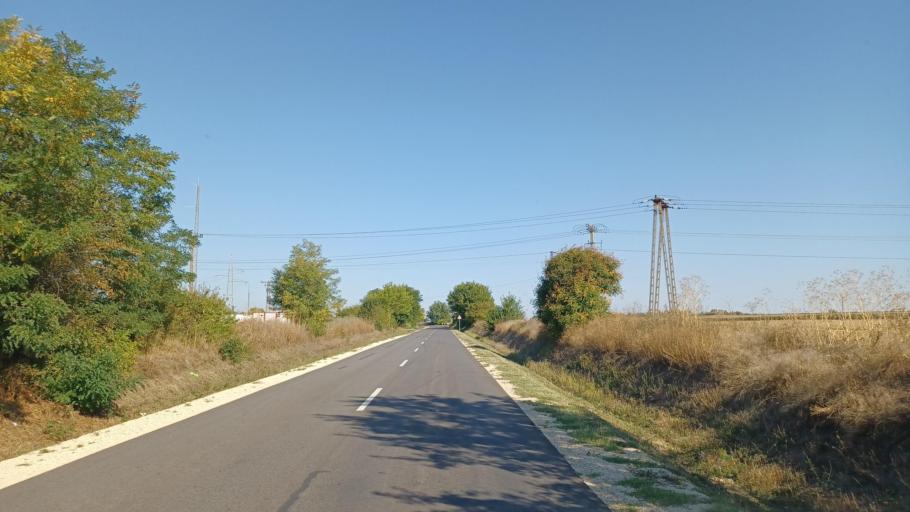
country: HU
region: Tolna
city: Paks
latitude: 46.6449
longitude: 18.8459
